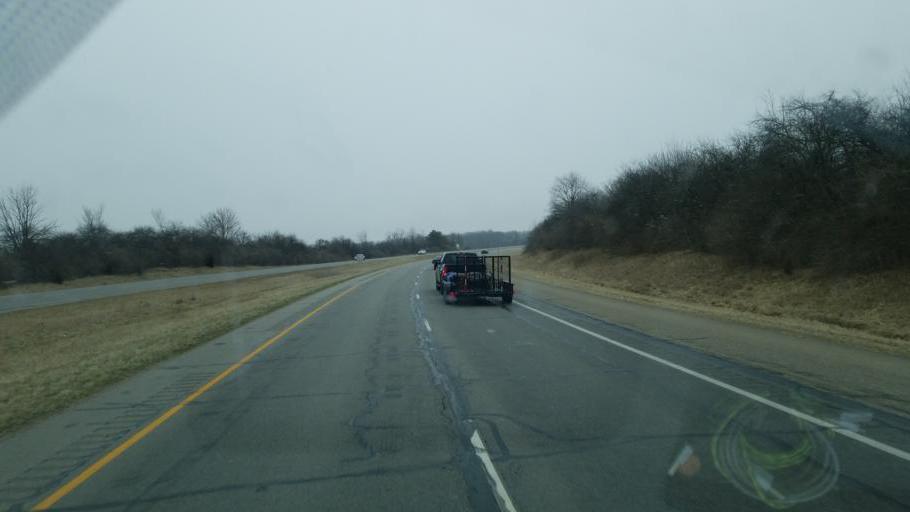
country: US
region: Indiana
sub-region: Miami County
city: Peru
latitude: 40.8057
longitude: -86.0216
